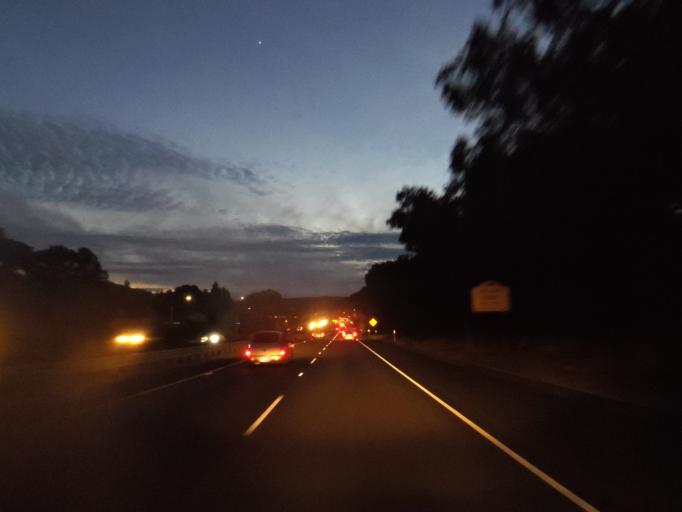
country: US
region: California
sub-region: San Luis Obispo County
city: San Luis Obispo
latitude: 35.2882
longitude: -120.6618
